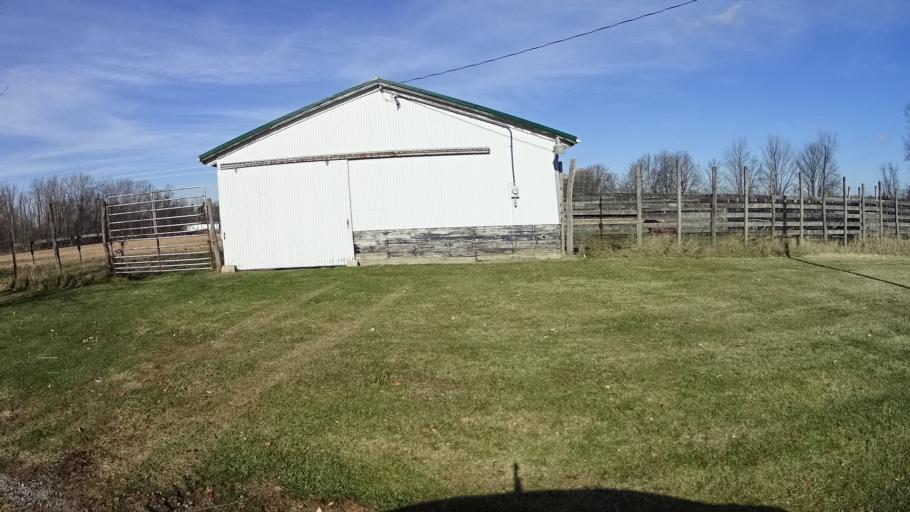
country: US
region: Ohio
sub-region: Lorain County
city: Wellington
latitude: 41.0859
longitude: -82.2768
